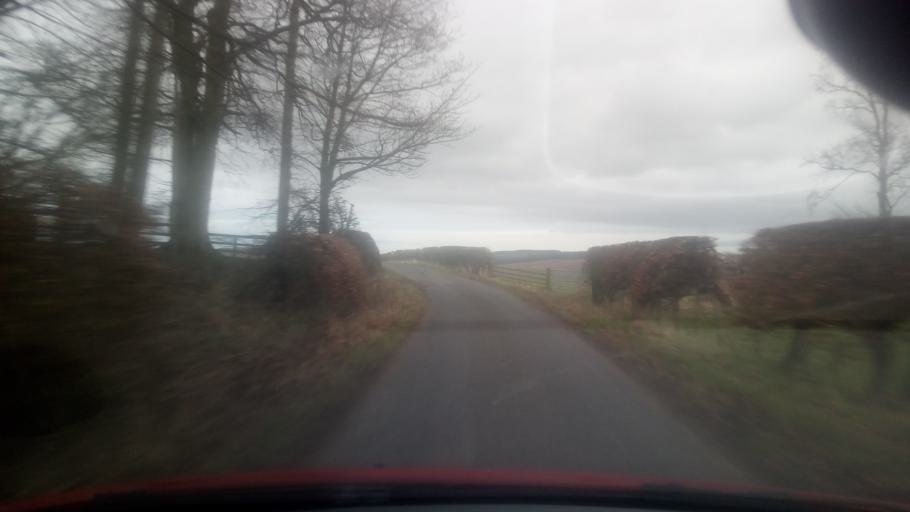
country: GB
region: Scotland
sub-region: The Scottish Borders
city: Jedburgh
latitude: 55.4648
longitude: -2.5028
